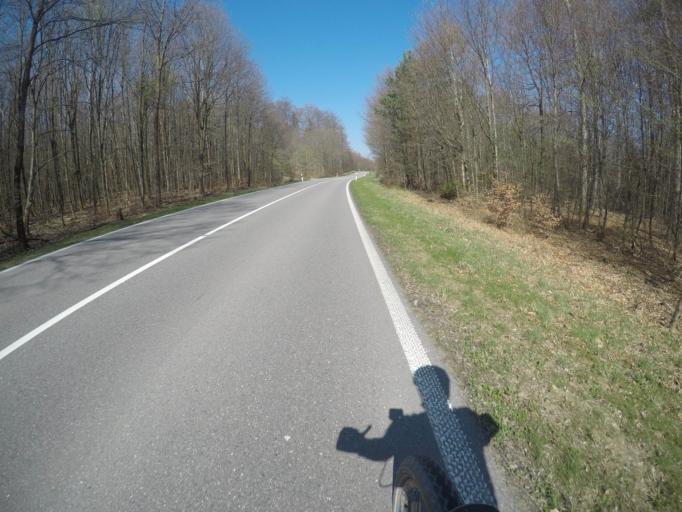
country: DE
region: Baden-Wuerttemberg
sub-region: Regierungsbezirk Stuttgart
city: Leonberg
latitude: 48.7561
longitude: 9.0155
